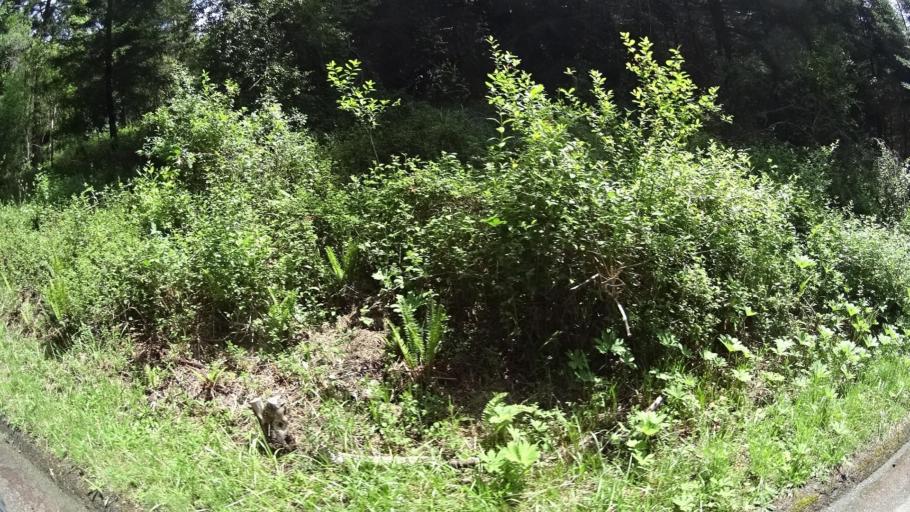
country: US
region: California
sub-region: Humboldt County
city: Arcata
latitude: 40.9101
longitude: -124.0456
